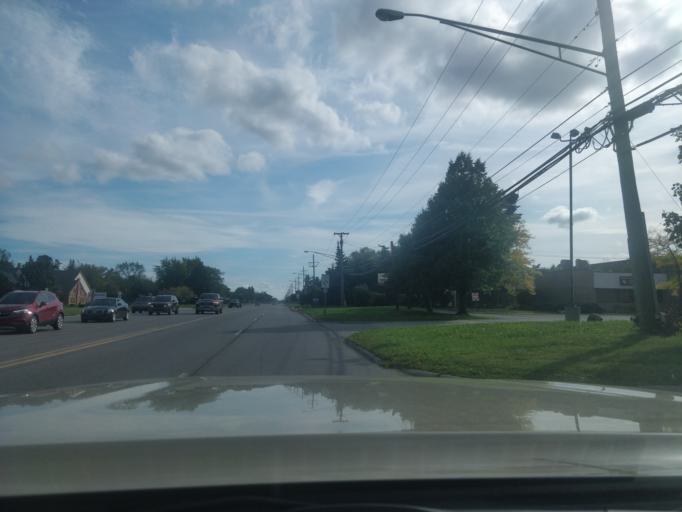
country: US
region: Michigan
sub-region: Wayne County
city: Woodhaven
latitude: 42.1691
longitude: -83.2271
